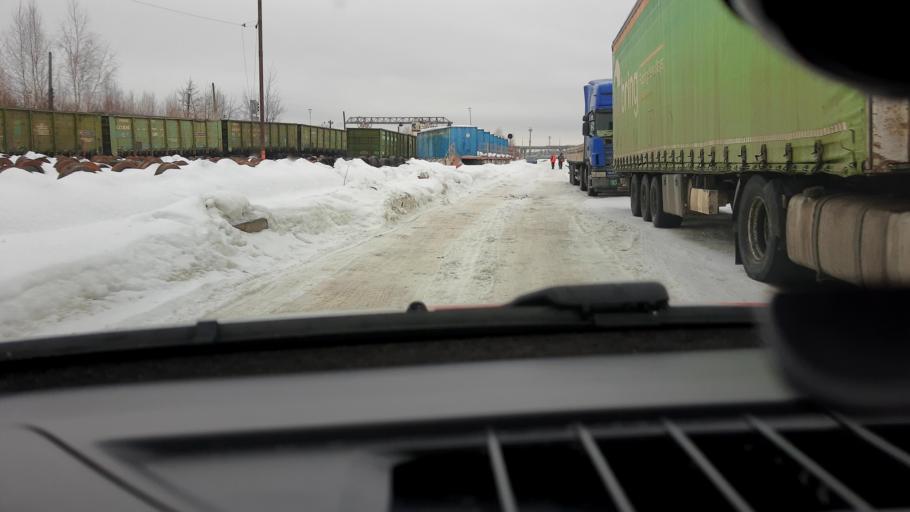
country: RU
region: Nizjnij Novgorod
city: Gorbatovka
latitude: 56.2824
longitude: 43.8509
